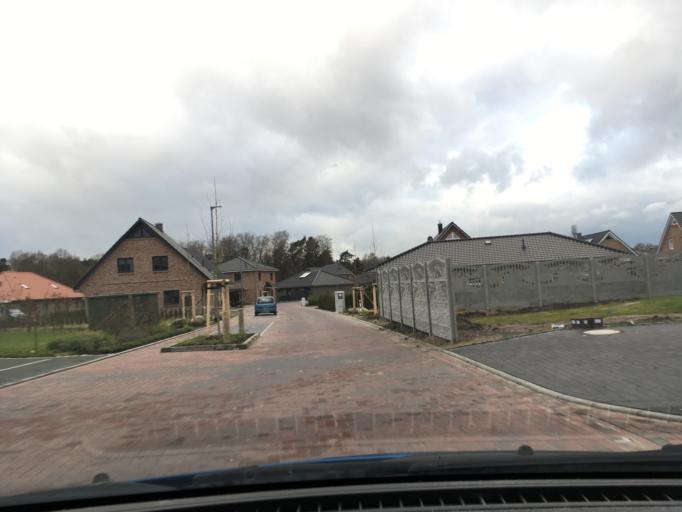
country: DE
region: Schleswig-Holstein
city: Kremperheide
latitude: 53.8977
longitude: 9.4979
